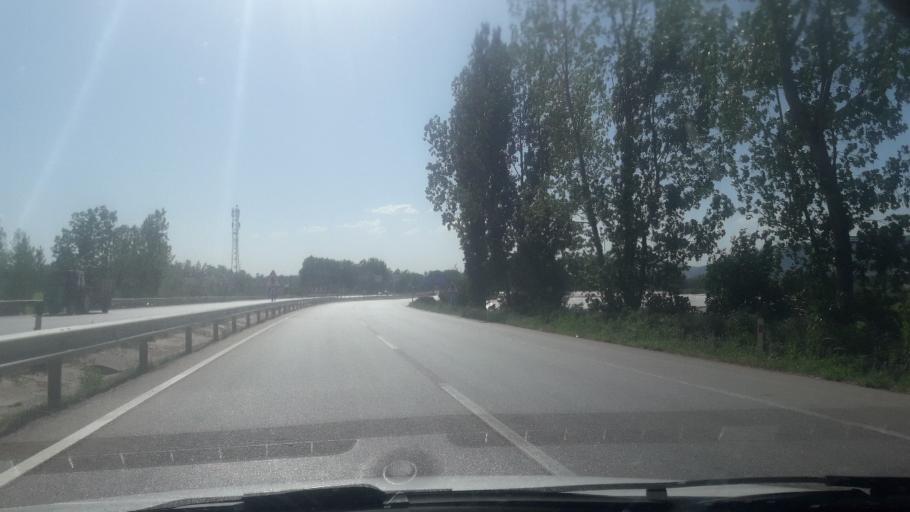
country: TR
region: Tokat
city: Yesilyurt
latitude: 40.2984
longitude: 36.3645
